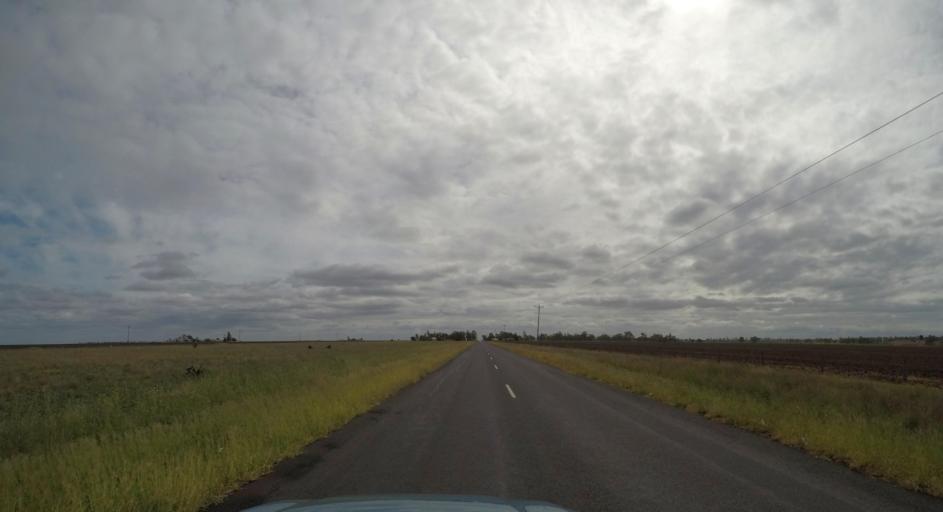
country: AU
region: Queensland
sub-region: Western Downs
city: Dalby
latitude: -26.9709
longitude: 151.2203
